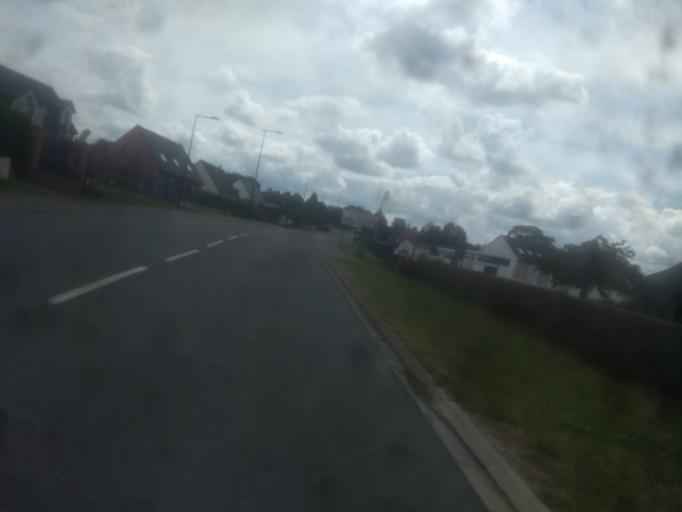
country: FR
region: Nord-Pas-de-Calais
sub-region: Departement du Pas-de-Calais
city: Duisans
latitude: 50.3341
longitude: 2.6430
